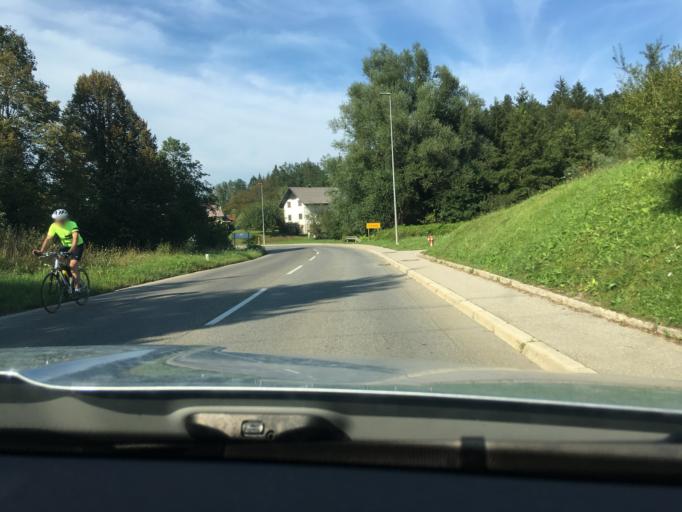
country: SI
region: Crnomelj
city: Crnomelj
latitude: 45.5619
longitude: 15.1713
